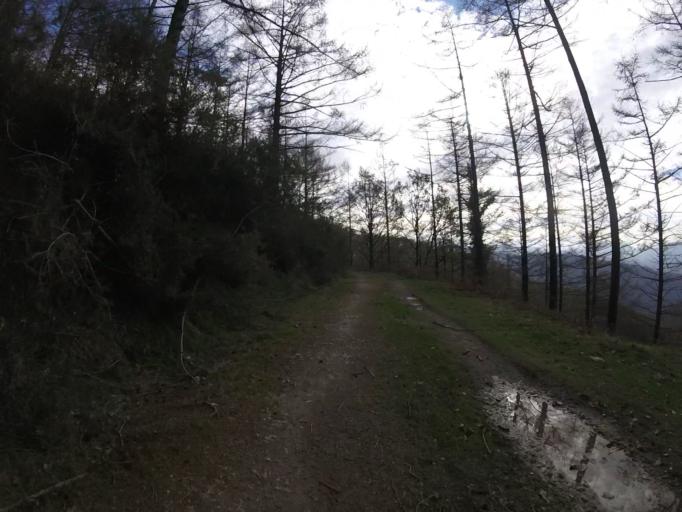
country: ES
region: Navarre
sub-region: Provincia de Navarra
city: Arano
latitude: 43.2418
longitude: -1.8500
